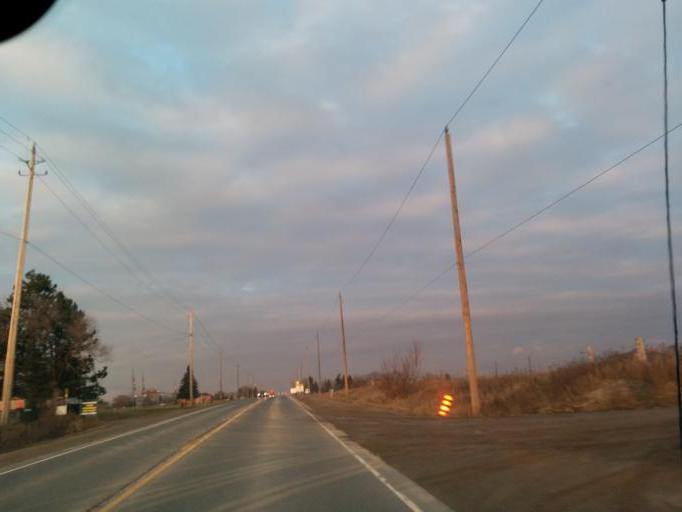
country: CA
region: Ontario
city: Brampton
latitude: 43.8337
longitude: -79.7116
